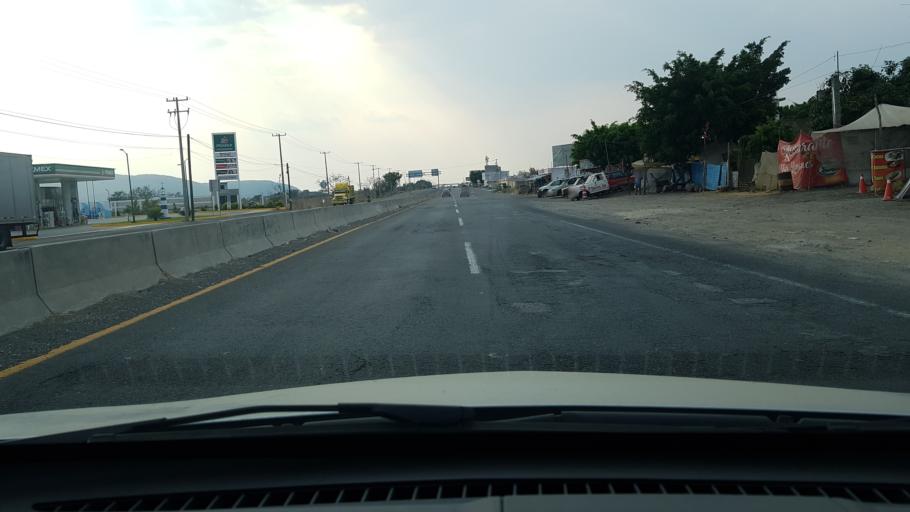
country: MX
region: Morelos
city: Amayuca
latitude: 18.7339
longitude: -98.8176
